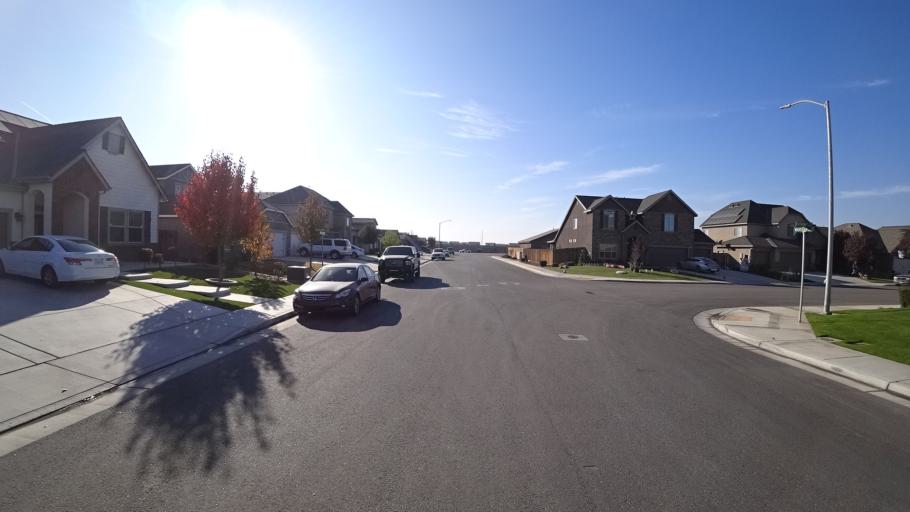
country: US
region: California
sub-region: Kern County
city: Greenfield
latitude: 35.2691
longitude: -119.0682
